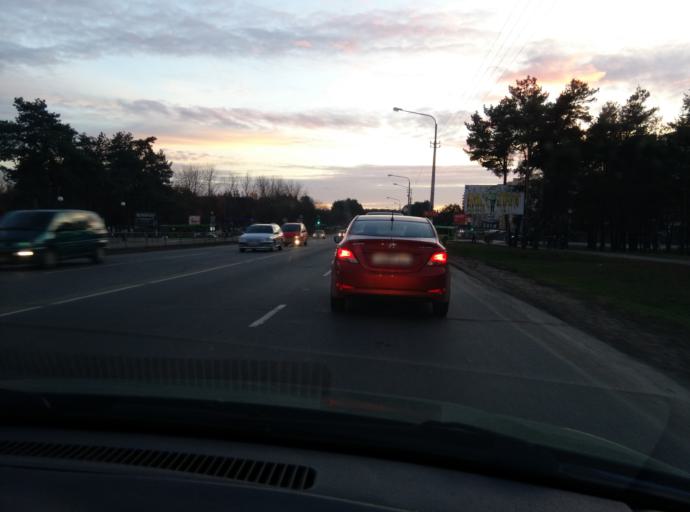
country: BY
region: Minsk
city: Horad Barysaw
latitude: 54.2097
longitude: 28.4861
